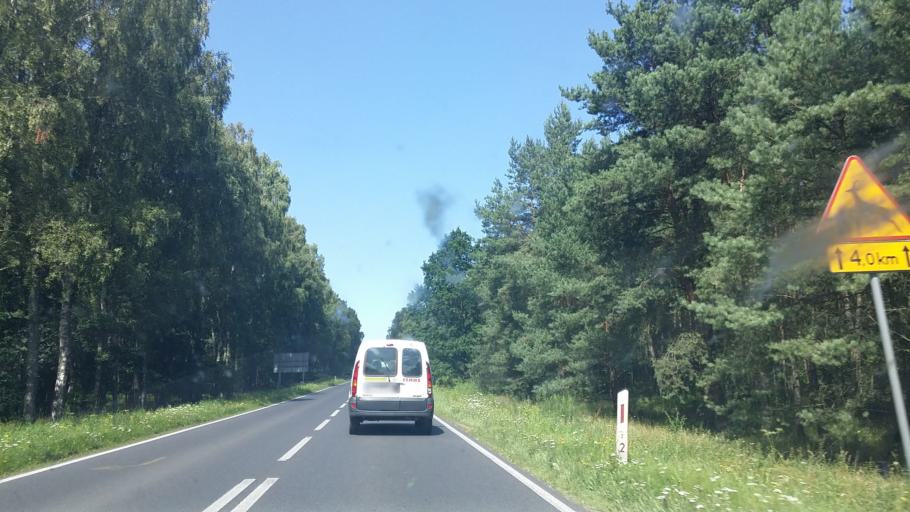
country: PL
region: West Pomeranian Voivodeship
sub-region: Powiat kolobrzeski
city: Kolobrzeg
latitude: 54.1181
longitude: 15.5879
